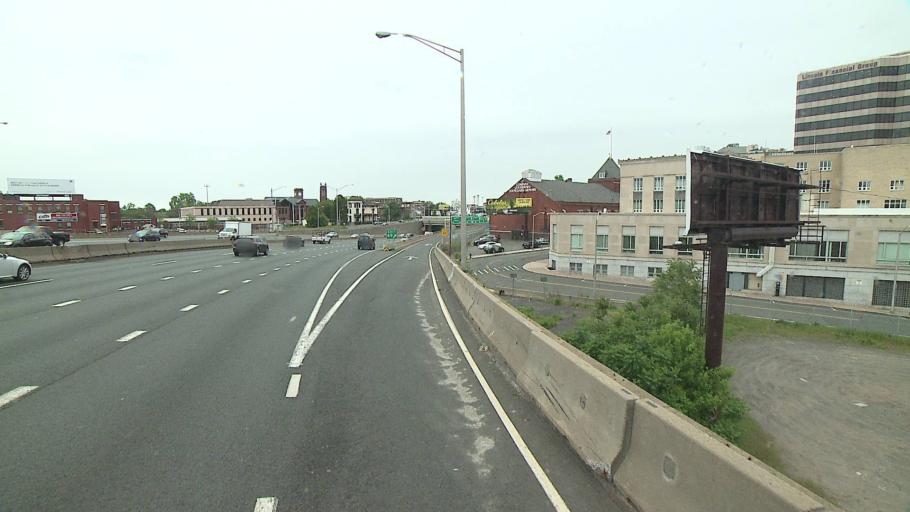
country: US
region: Connecticut
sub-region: Hartford County
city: Hartford
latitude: 41.7705
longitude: -72.6815
